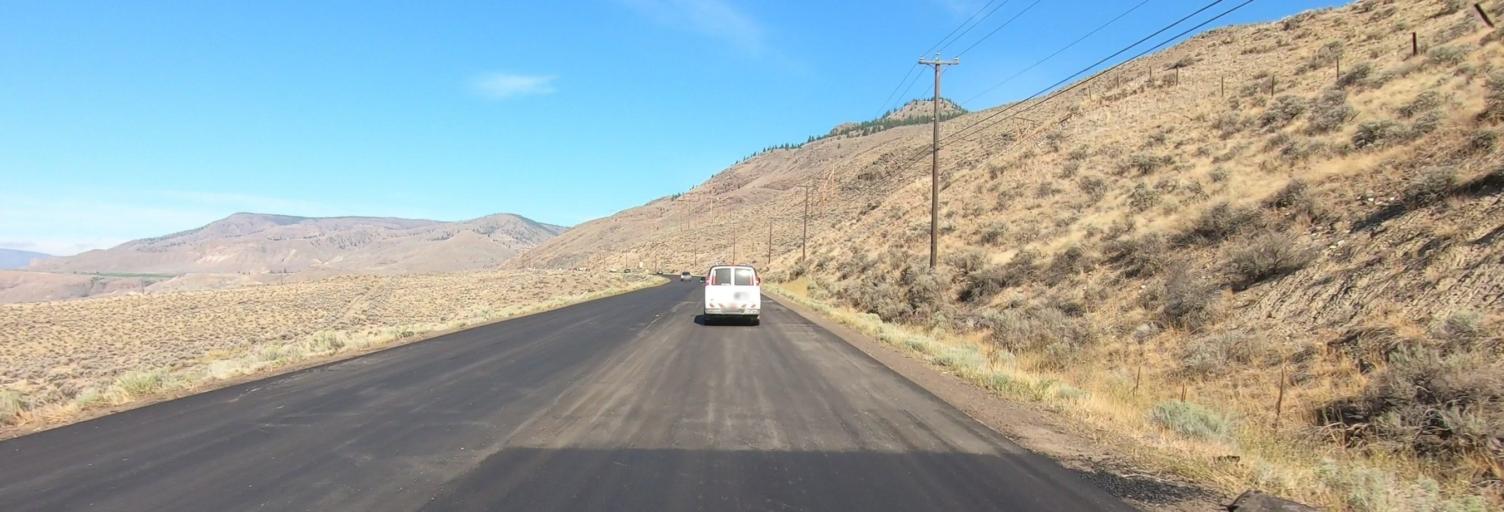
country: CA
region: British Columbia
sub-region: Thompson-Nicola Regional District
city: Ashcroft
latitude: 50.7852
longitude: -121.0656
